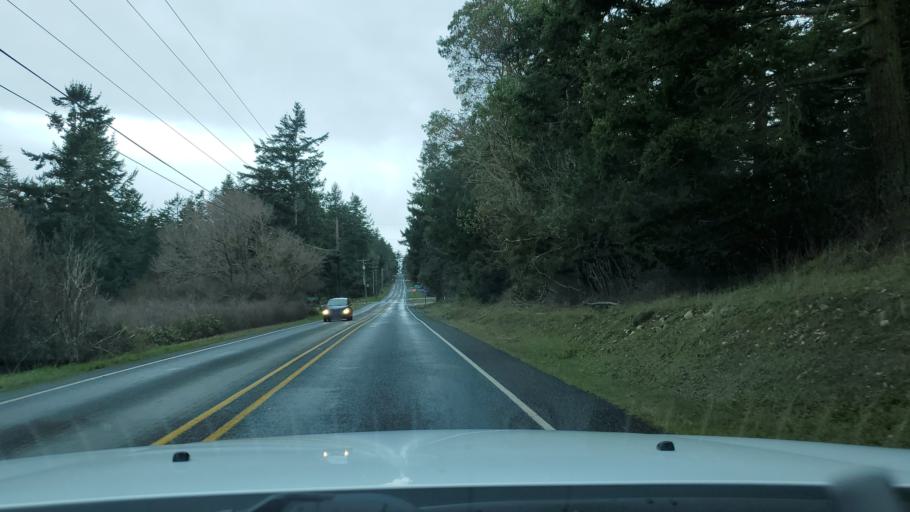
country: US
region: Washington
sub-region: Island County
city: Coupeville
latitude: 48.2319
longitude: -122.7560
